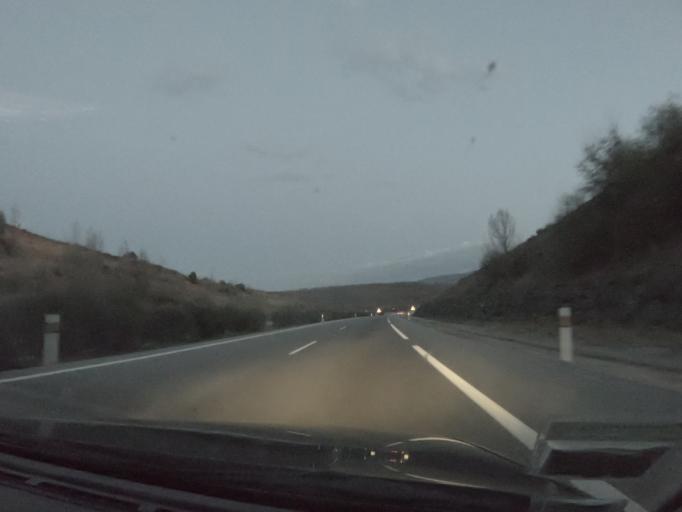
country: ES
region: Castille and Leon
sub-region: Provincia de Leon
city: Bembibre
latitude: 42.6253
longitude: -6.4119
